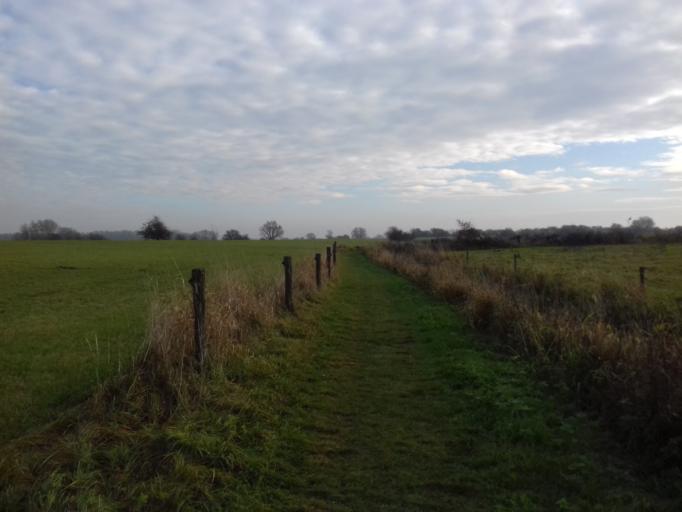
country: NL
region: Gelderland
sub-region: Gemeente Neerijnen
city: Neerijnen
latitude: 51.8252
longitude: 5.2701
